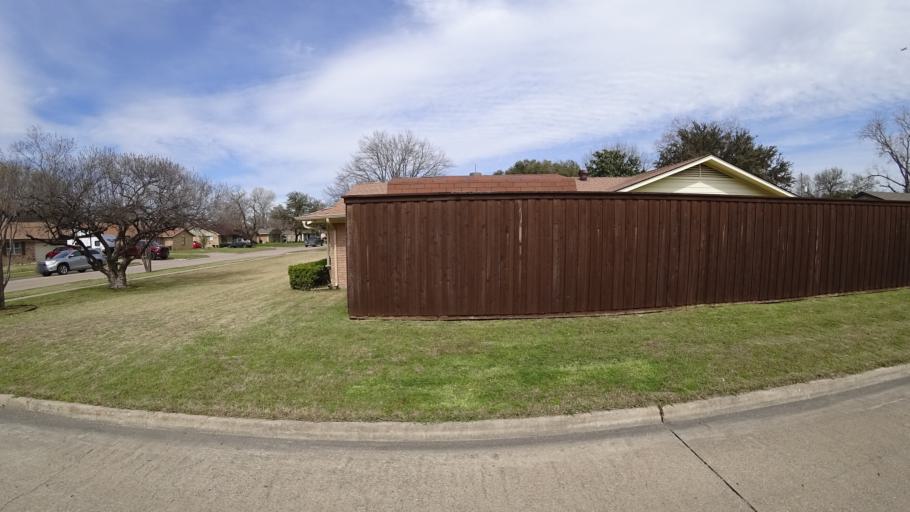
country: US
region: Texas
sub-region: Denton County
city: Lewisville
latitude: 33.0396
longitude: -97.0140
